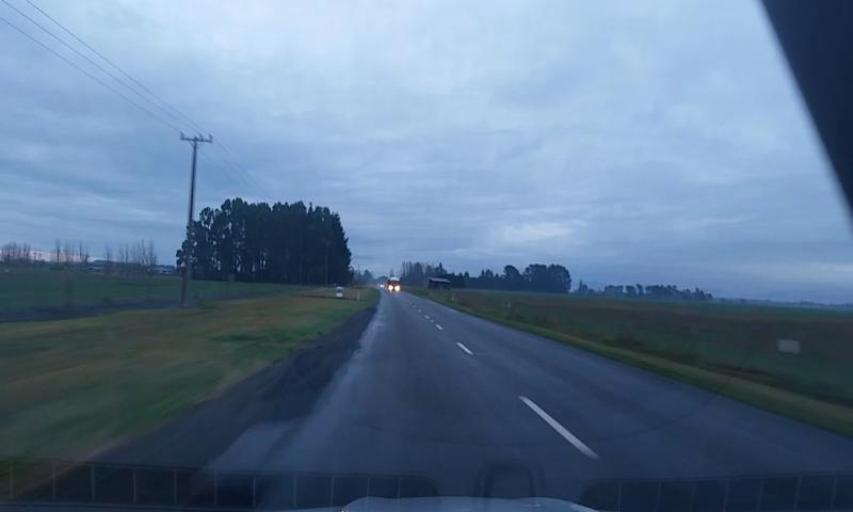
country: NZ
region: Canterbury
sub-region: Ashburton District
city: Rakaia
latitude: -43.7585
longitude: 171.9691
